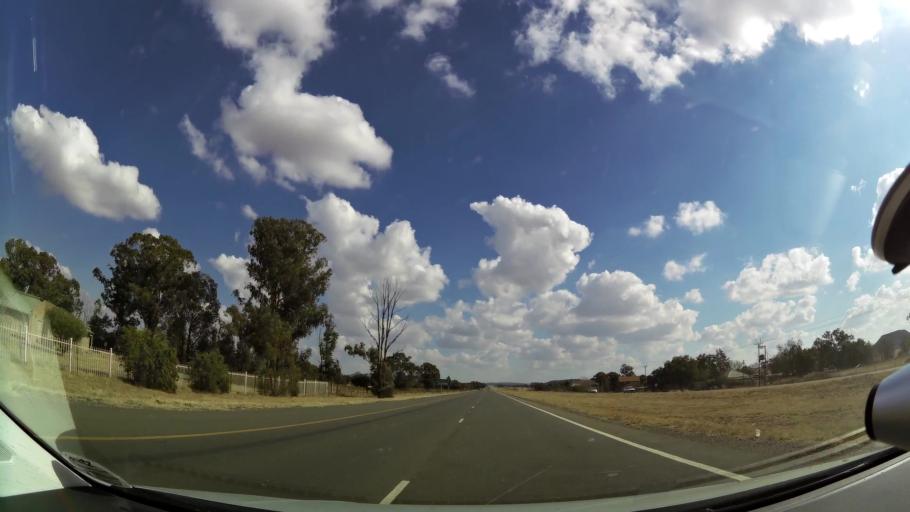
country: ZA
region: Orange Free State
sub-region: Mangaung Metropolitan Municipality
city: Bloemfontein
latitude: -29.1336
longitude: 26.1397
